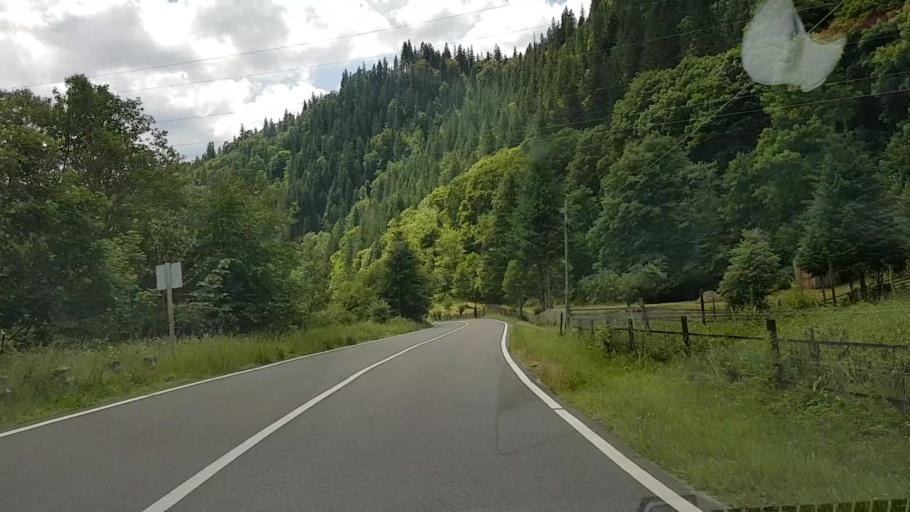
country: RO
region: Suceava
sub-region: Comuna Crucea
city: Crucea
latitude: 47.3193
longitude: 25.6271
